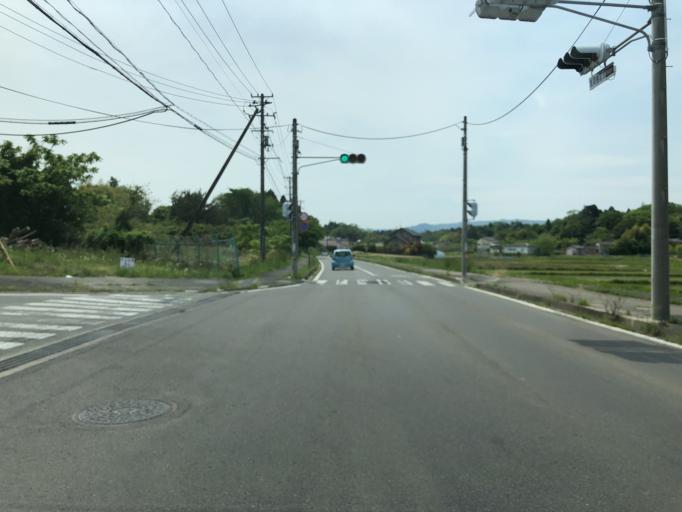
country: JP
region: Miyagi
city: Marumori
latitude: 37.8186
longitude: 140.9374
